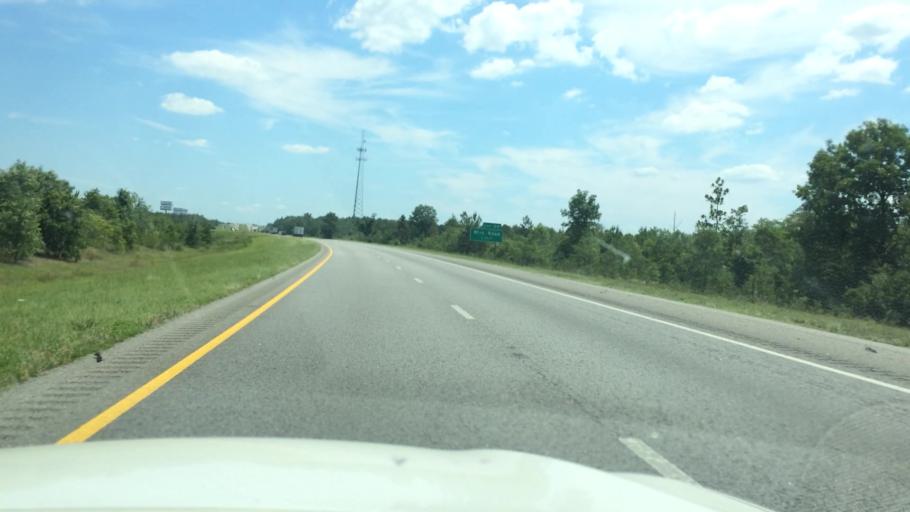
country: US
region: South Carolina
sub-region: Aiken County
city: Aiken
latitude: 33.7095
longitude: -81.5847
